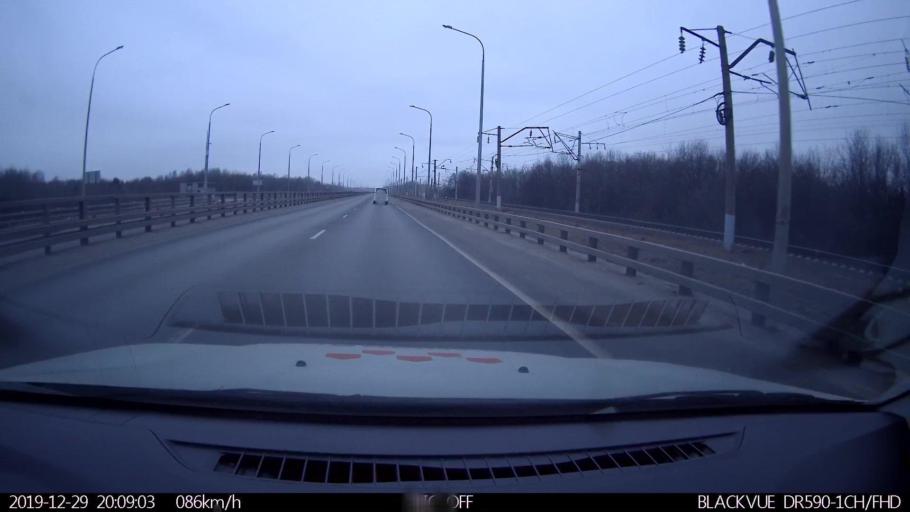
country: RU
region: Nizjnij Novgorod
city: Neklyudovo
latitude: 56.3791
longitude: 43.9566
